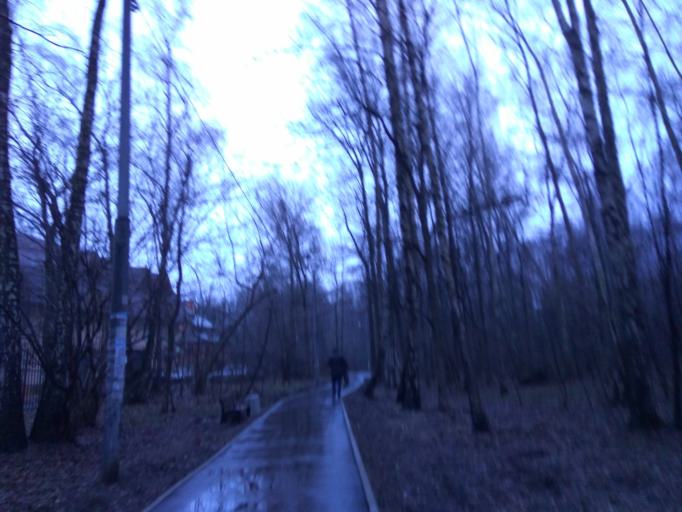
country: RU
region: Moscow
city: Vagonoremont
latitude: 55.9012
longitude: 37.5583
